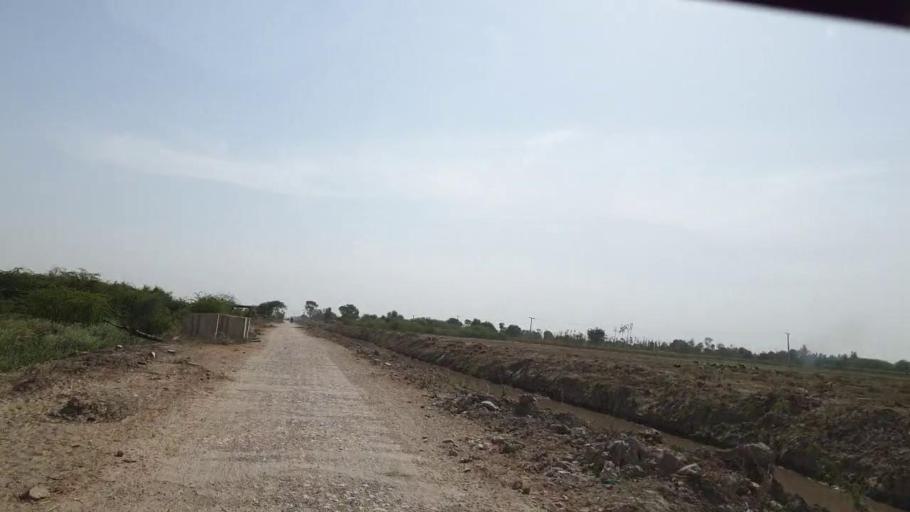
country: PK
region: Sindh
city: Nabisar
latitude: 25.0793
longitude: 69.5798
